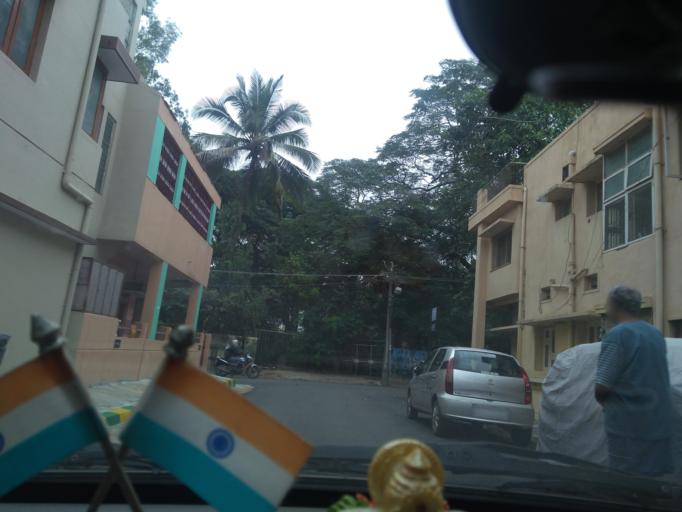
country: IN
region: Karnataka
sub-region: Bangalore Urban
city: Bangalore
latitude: 12.9884
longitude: 77.5518
